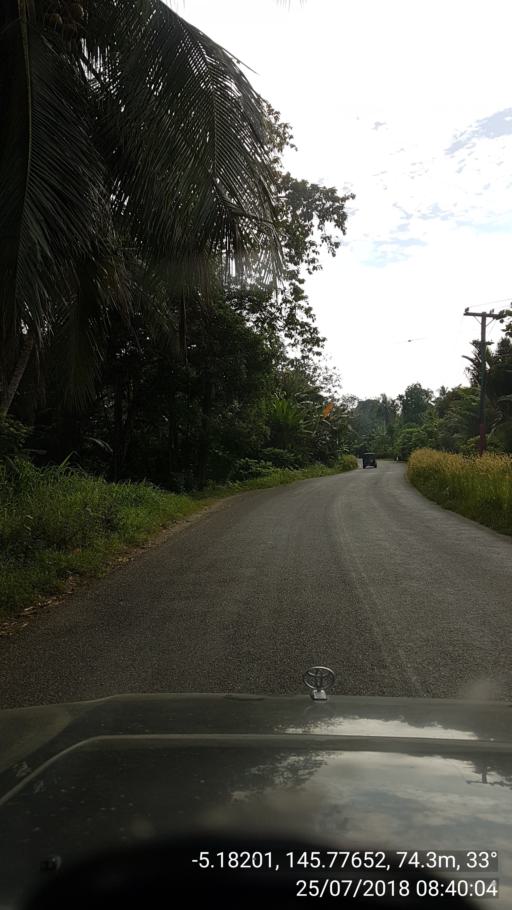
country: PG
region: Madang
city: Madang
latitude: -5.1819
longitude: 145.7764
